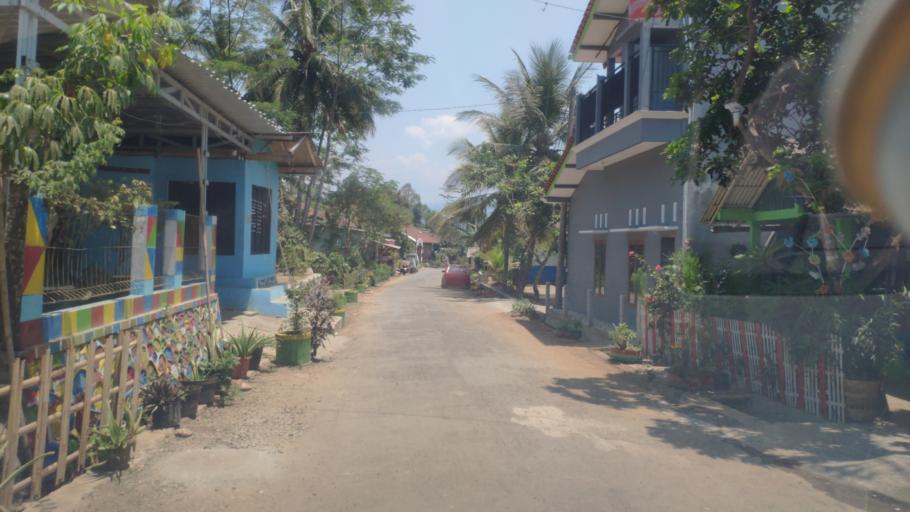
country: ID
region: Central Java
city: Wonosobo
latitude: -7.4054
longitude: 109.6714
